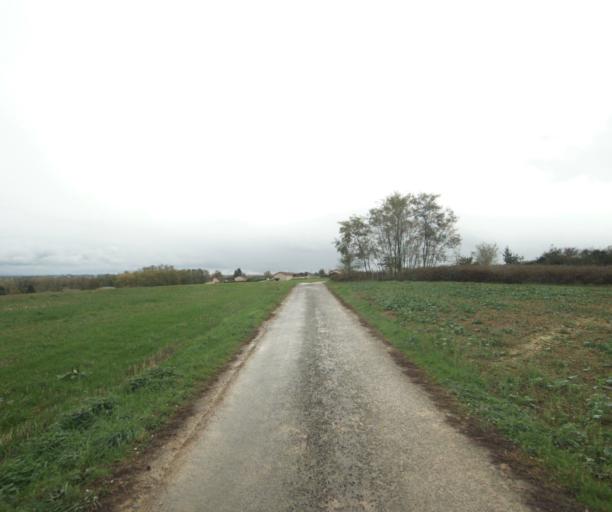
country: FR
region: Rhone-Alpes
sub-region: Departement de l'Ain
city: Pont-de-Vaux
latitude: 46.4554
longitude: 4.8811
